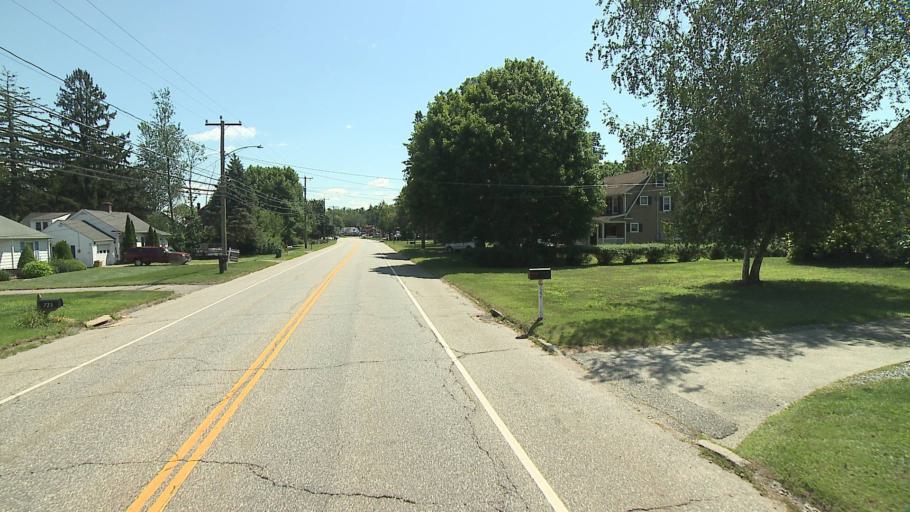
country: US
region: Connecticut
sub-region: Litchfield County
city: Torrington
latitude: 41.8032
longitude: -73.0924
